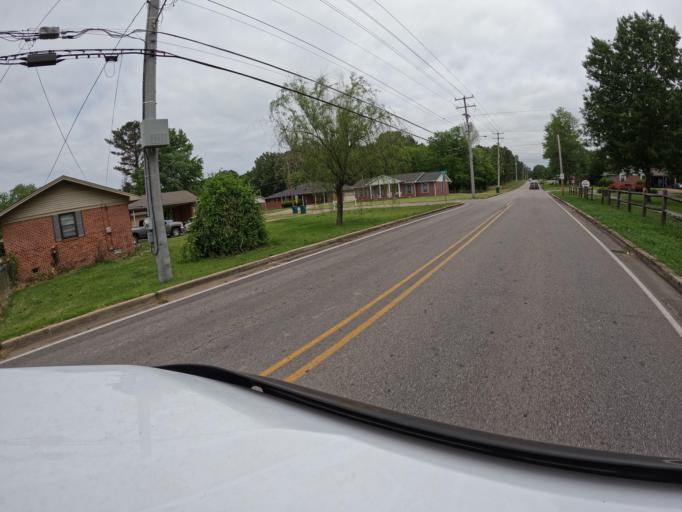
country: US
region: Mississippi
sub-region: Lee County
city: Tupelo
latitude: 34.2676
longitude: -88.7377
